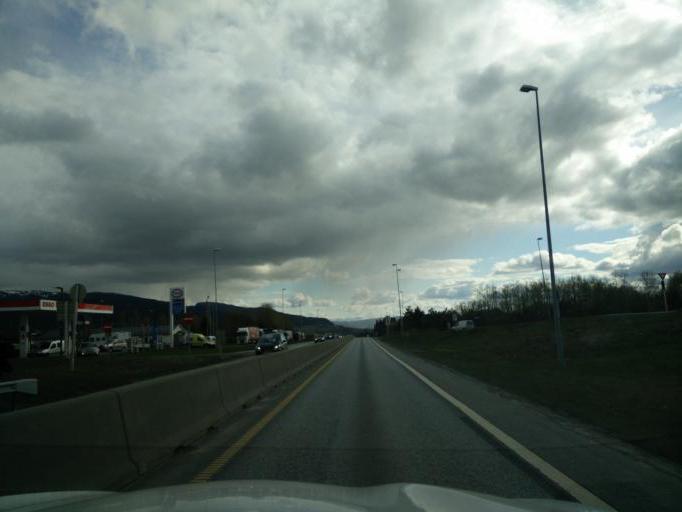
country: NO
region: Sor-Trondelag
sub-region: Melhus
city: Melhus
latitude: 63.3332
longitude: 10.3559
